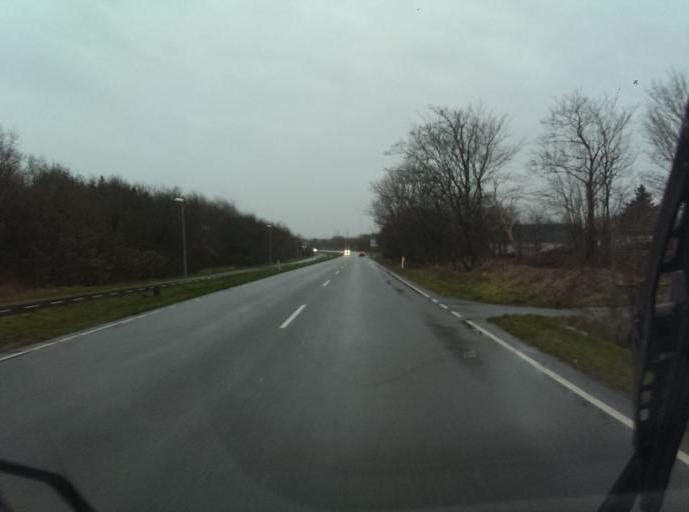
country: DK
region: South Denmark
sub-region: Esbjerg Kommune
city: Esbjerg
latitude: 55.4877
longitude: 8.5120
